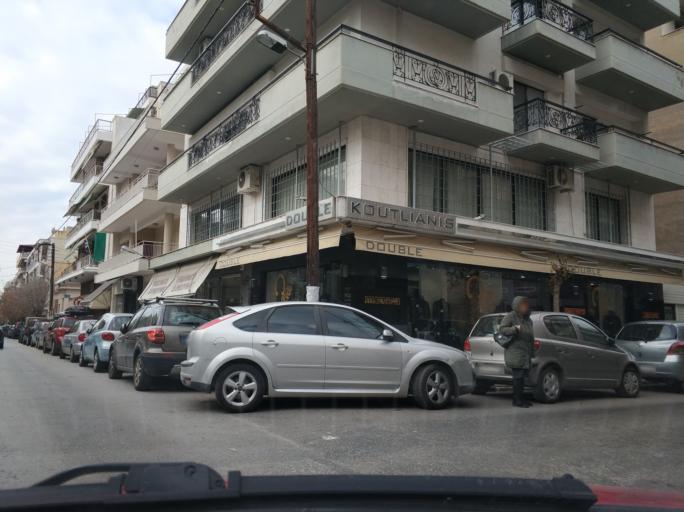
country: GR
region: Central Macedonia
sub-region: Nomos Thessalonikis
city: Triandria
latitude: 40.6024
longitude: 22.9680
